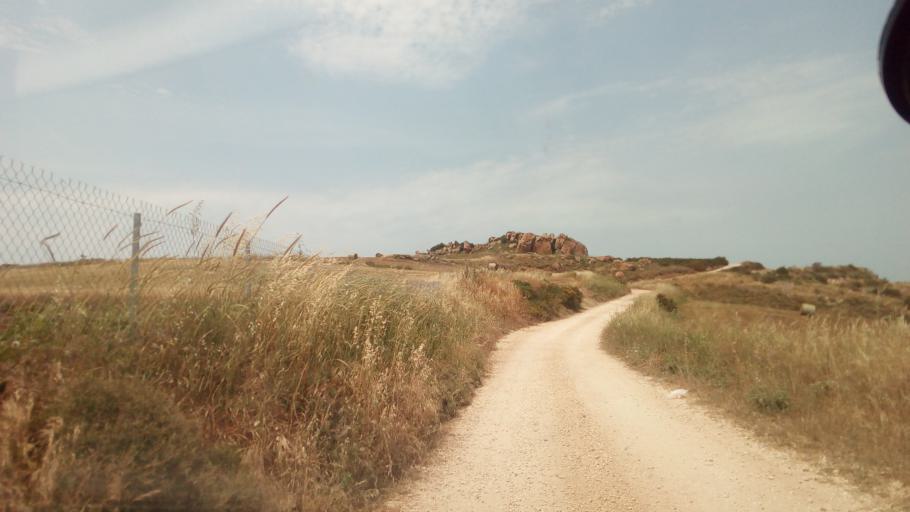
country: CY
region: Pafos
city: Polis
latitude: 34.9806
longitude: 32.3558
